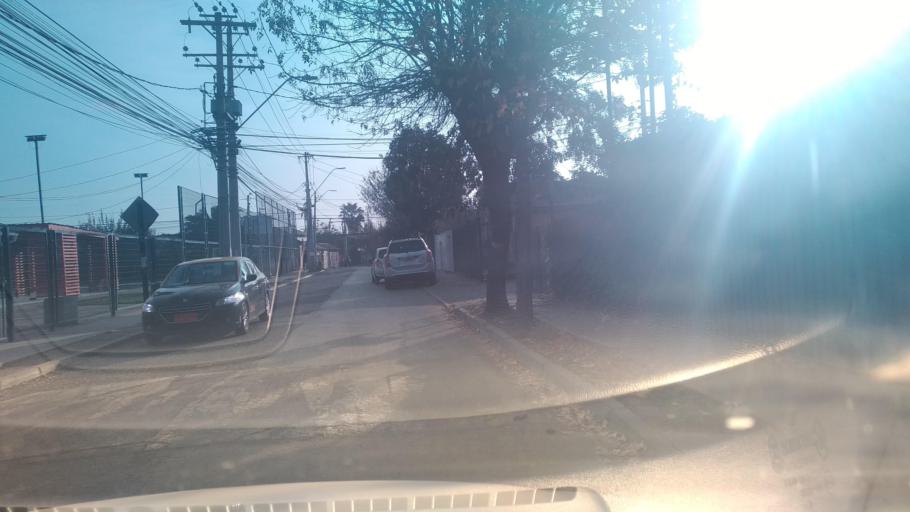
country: CL
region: Santiago Metropolitan
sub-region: Provincia de Santiago
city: Lo Prado
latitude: -33.3612
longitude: -70.7142
